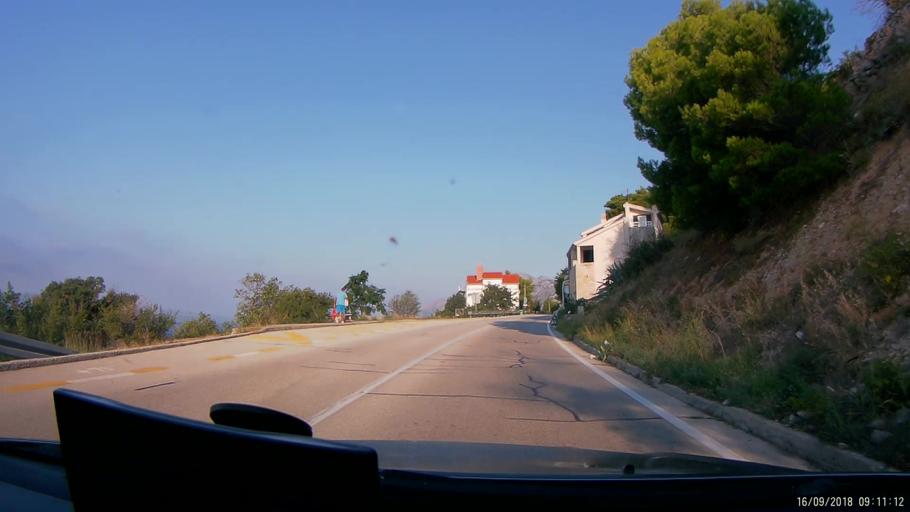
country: HR
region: Splitsko-Dalmatinska
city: Donja Brela
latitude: 43.3845
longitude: 16.9126
